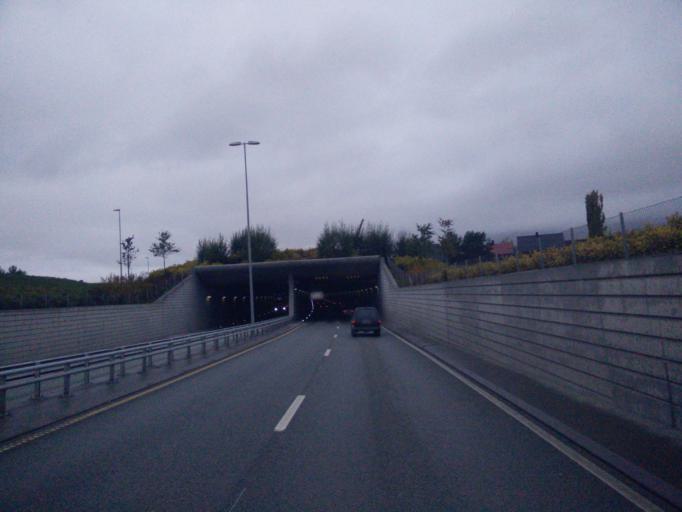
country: NO
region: Nord-Trondelag
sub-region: Stjordal
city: Stjordal
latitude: 63.4687
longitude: 10.9105
